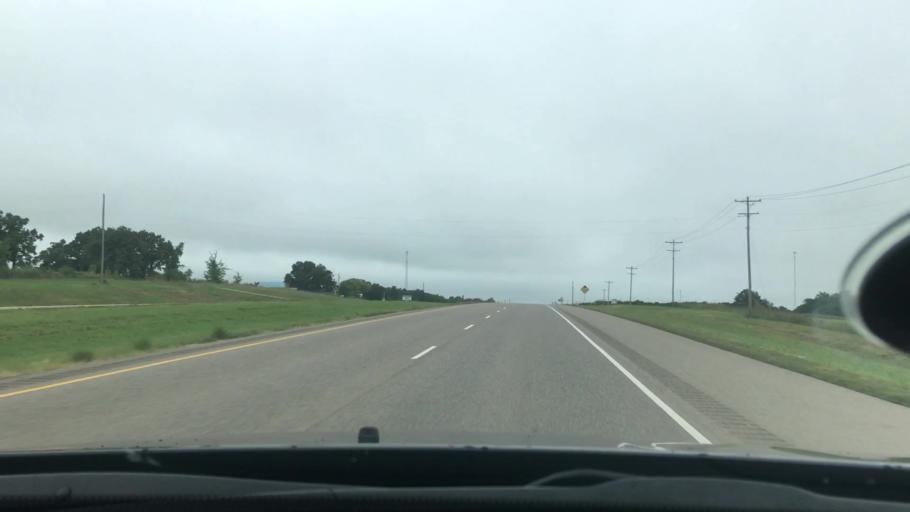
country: US
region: Oklahoma
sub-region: Lincoln County
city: Prague
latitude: 35.3683
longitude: -96.6714
